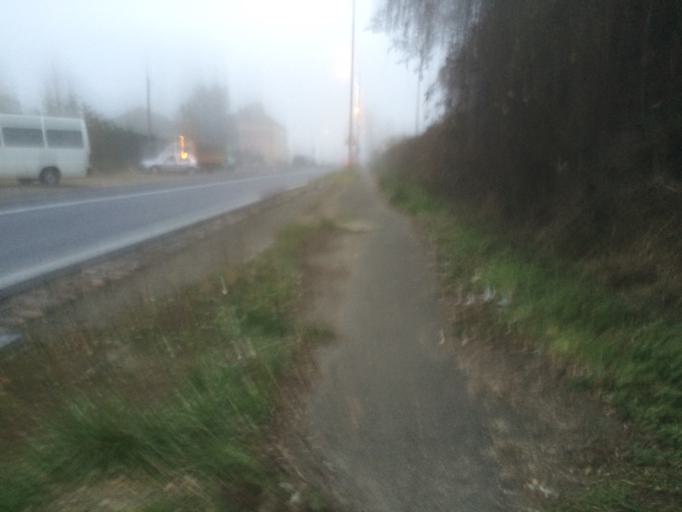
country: FR
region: Ile-de-France
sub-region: Departement de l'Essonne
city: Saclay
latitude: 48.7319
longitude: 2.1658
